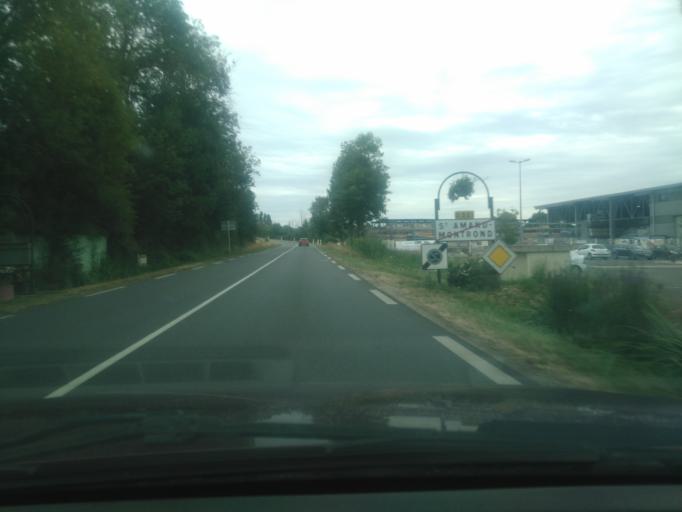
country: FR
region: Centre
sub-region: Departement du Cher
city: Saint-Amand-Montrond
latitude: 46.7221
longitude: 2.5381
